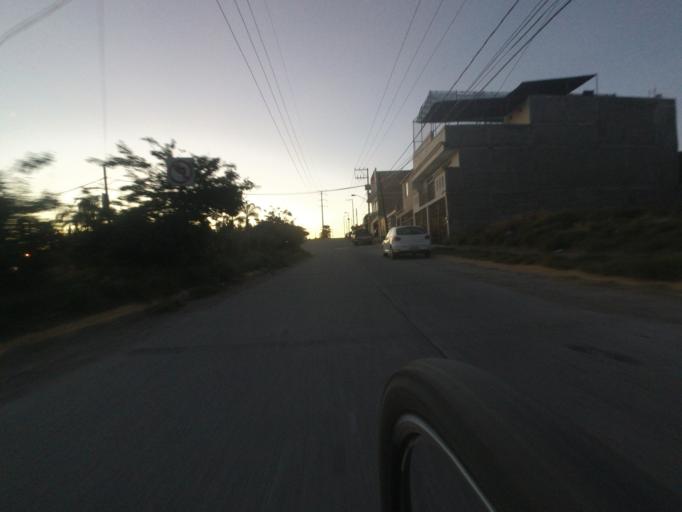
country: MX
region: Aguascalientes
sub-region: Aguascalientes
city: La Loma de los Negritos
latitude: 21.8539
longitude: -102.3330
